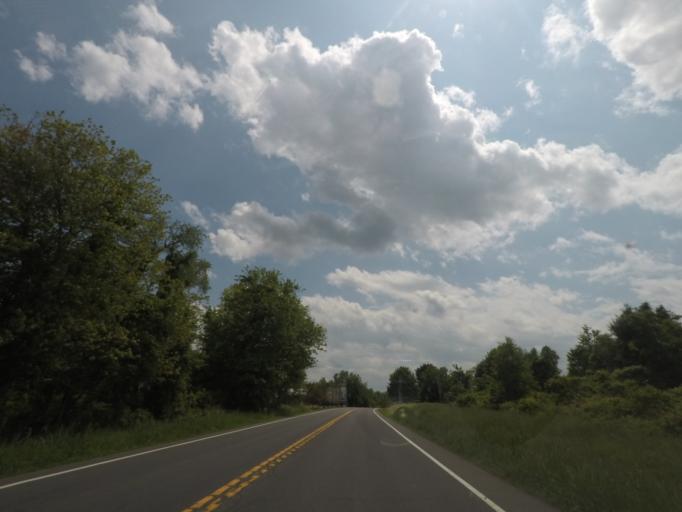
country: US
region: New York
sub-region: Columbia County
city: Oakdale
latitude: 42.2051
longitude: -73.7308
